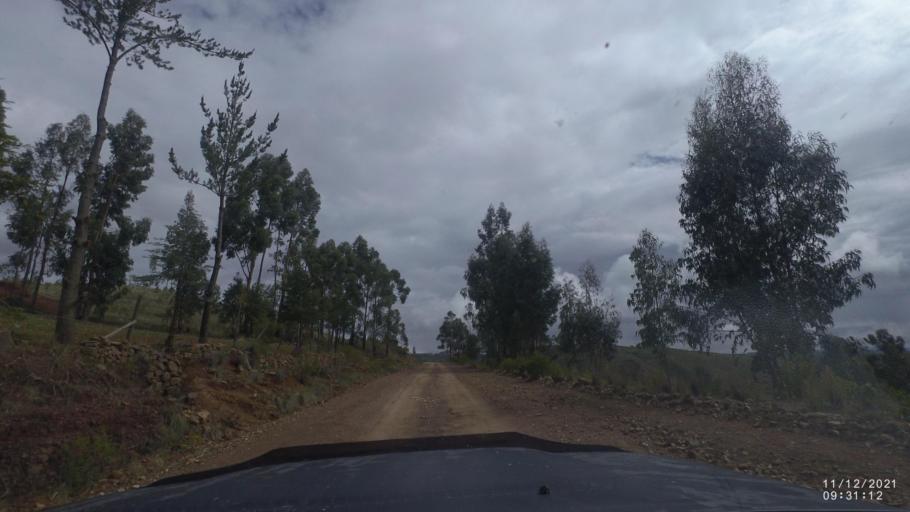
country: BO
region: Cochabamba
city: Tarata
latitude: -17.8544
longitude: -65.9884
